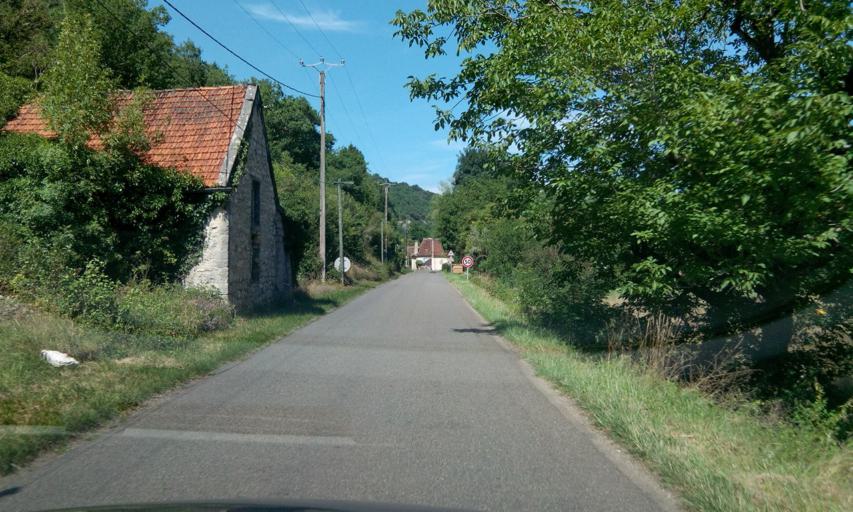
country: FR
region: Midi-Pyrenees
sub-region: Departement du Lot
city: Vayrac
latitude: 44.9256
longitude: 1.6431
